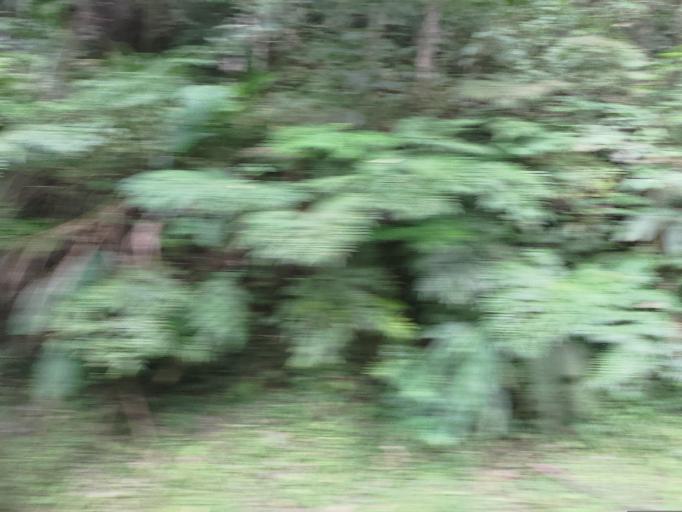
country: TW
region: Taiwan
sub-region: Hsinchu
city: Hsinchu
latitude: 24.6076
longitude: 121.0401
